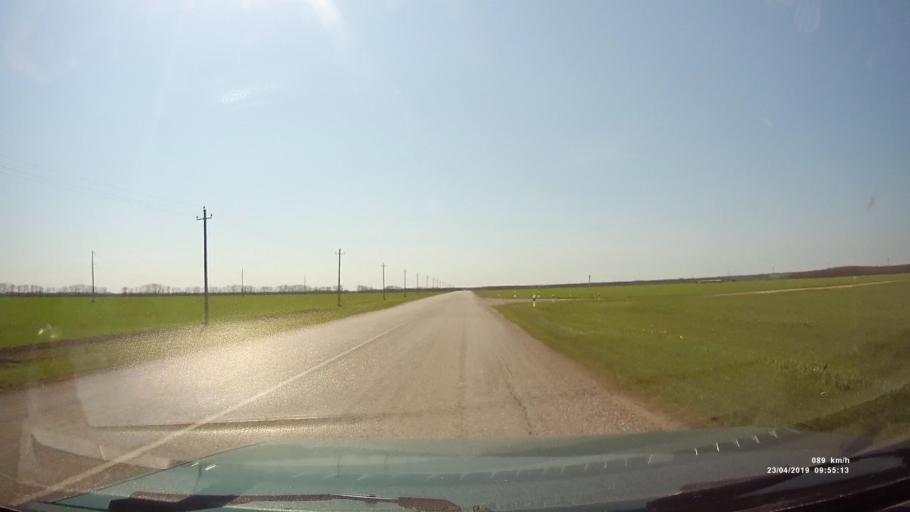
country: RU
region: Rostov
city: Orlovskiy
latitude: 46.8118
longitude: 42.0610
